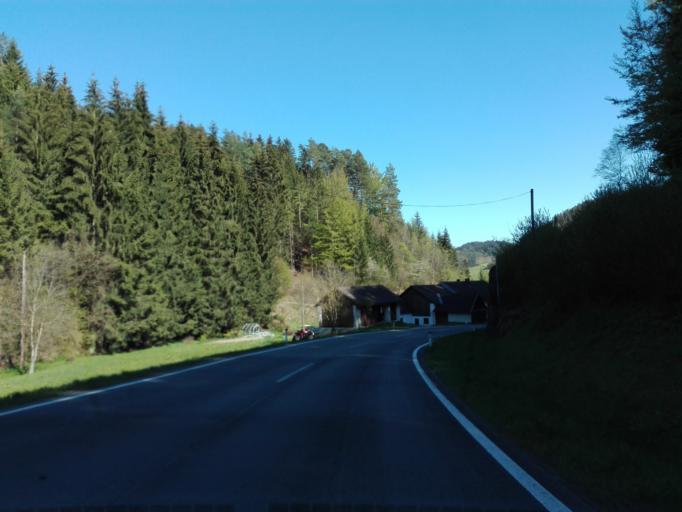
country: AT
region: Upper Austria
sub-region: Politischer Bezirk Perg
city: Perg
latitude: 48.3468
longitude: 14.7107
